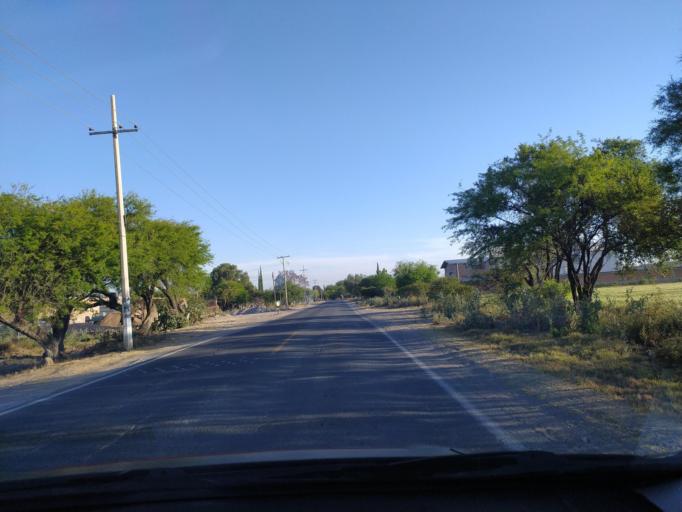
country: MX
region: Guanajuato
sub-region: San Francisco del Rincon
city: San Ignacio de Hidalgo
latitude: 20.9129
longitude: -101.8577
